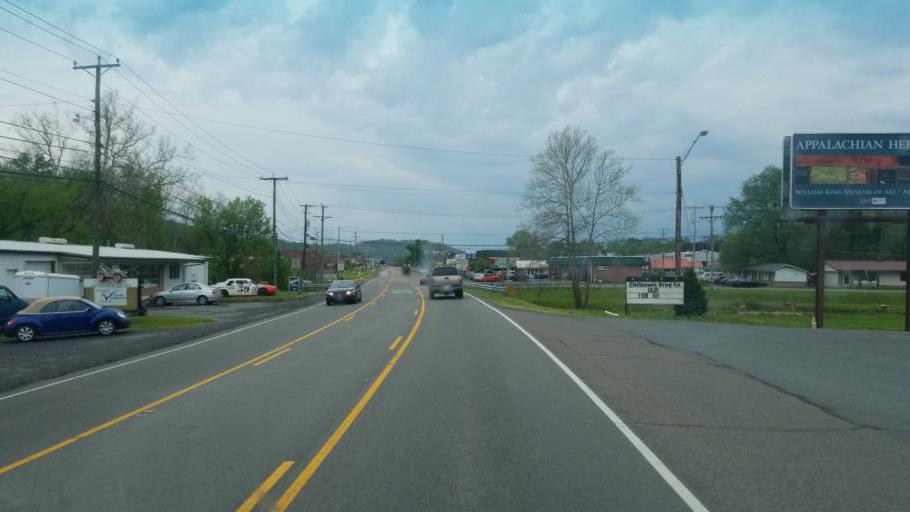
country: US
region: Virginia
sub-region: Smyth County
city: Chilhowie
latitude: 36.8078
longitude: -81.6717
